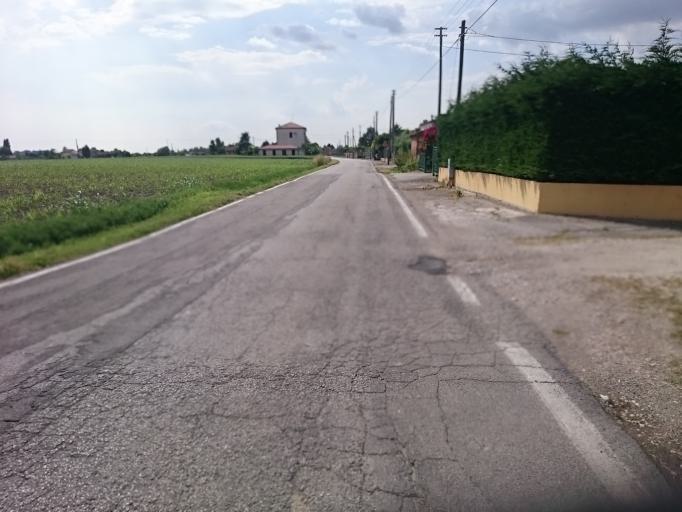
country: IT
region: Veneto
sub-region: Provincia di Padova
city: Casale di Scodosia
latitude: 45.1972
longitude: 11.4827
